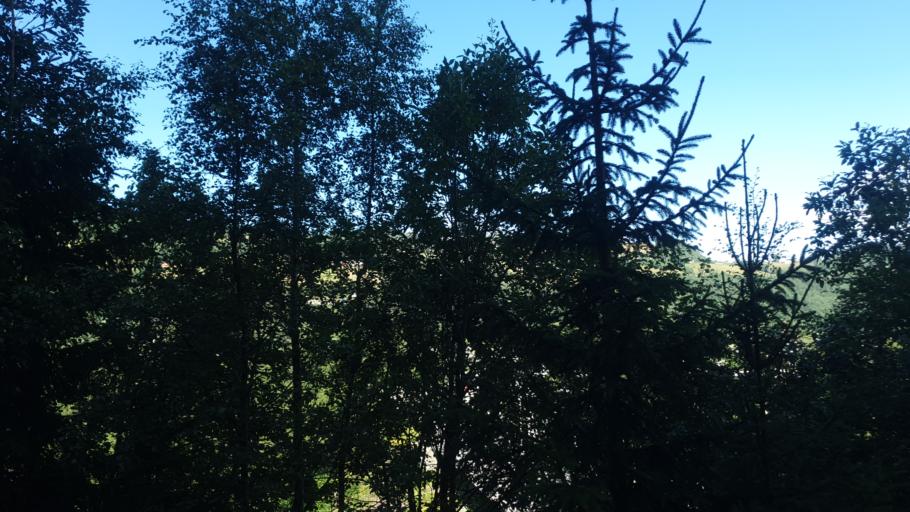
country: NO
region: Sor-Trondelag
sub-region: Meldal
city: Meldal
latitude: 63.1671
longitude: 9.7432
